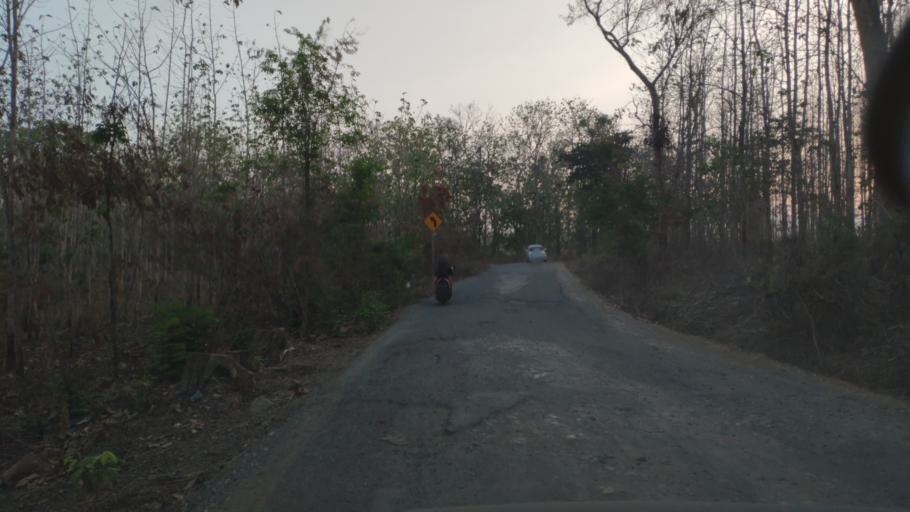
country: ID
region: Central Java
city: Semanggi
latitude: -7.0634
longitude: 111.4130
